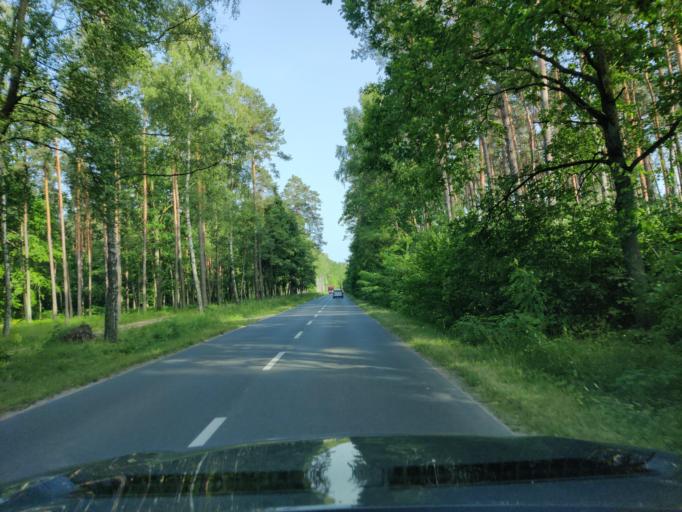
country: PL
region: Masovian Voivodeship
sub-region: Powiat wyszkowski
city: Wyszkow
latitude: 52.6613
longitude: 21.4386
